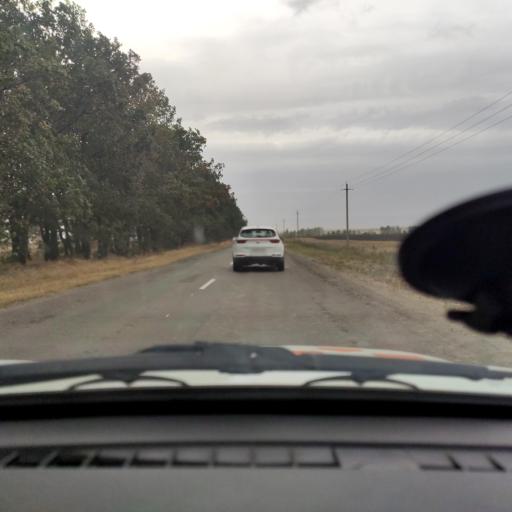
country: RU
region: Lipetsk
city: Khlevnoye
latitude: 52.0059
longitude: 39.1423
